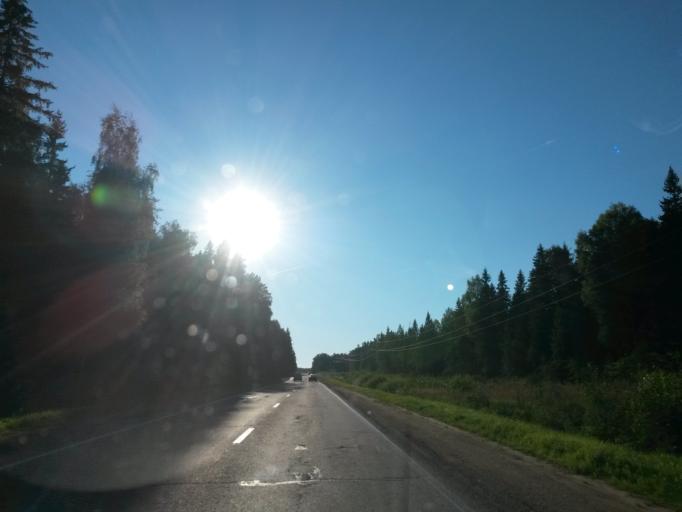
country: RU
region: Jaroslavl
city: Gavrilov-Yam
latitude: 57.2676
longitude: 39.9847
